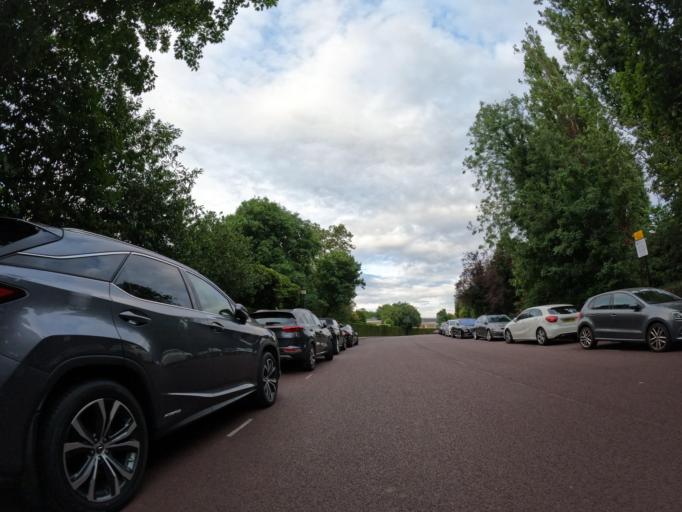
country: GB
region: England
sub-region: Greater London
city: Camden Town
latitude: 51.5291
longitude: -0.1535
